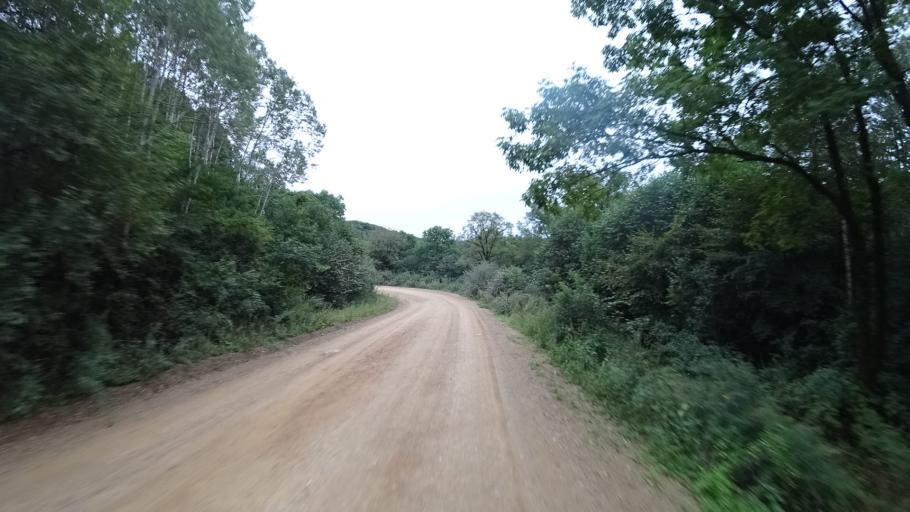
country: RU
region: Primorskiy
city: Rettikhovka
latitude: 44.1795
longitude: 132.8572
